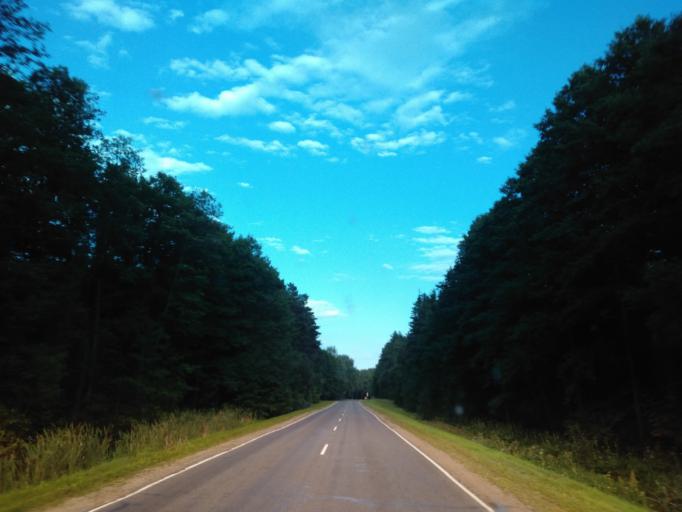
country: BY
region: Minsk
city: Uzda
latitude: 53.4233
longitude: 27.3894
